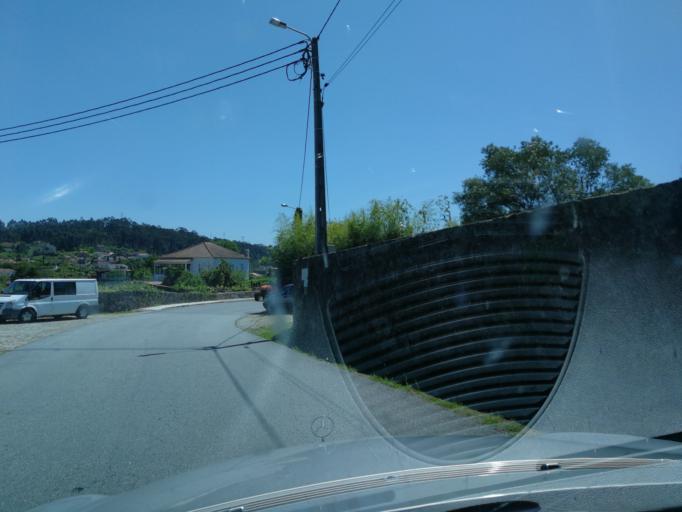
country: PT
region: Viana do Castelo
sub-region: Viana do Castelo
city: Meadela
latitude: 41.7365
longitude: -8.7857
